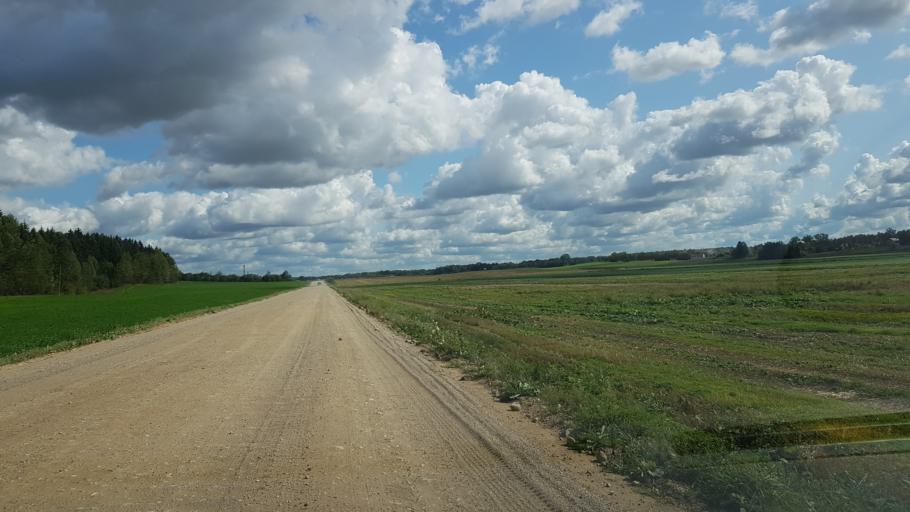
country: BY
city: Fanipol
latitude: 53.7376
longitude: 27.2725
